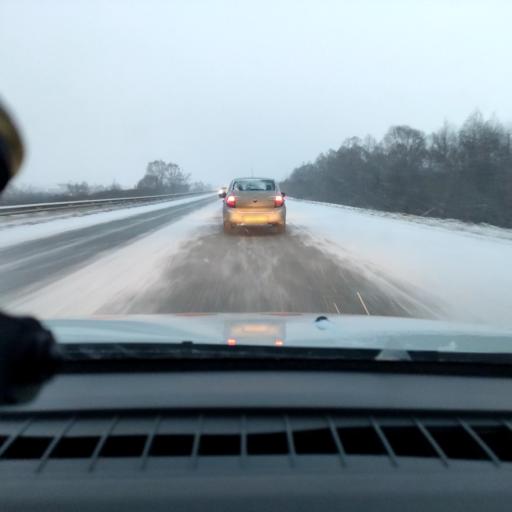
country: RU
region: Samara
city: Kinel'-Cherkassy
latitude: 53.4115
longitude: 51.4422
